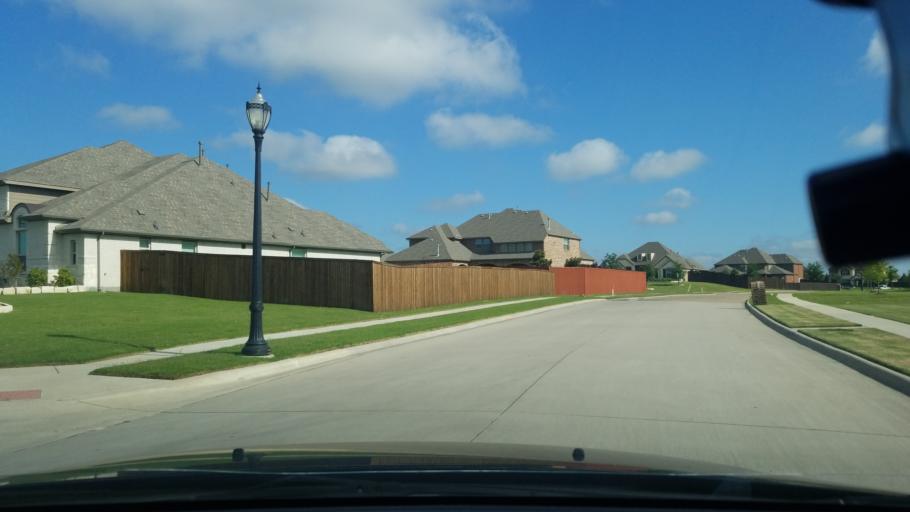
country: US
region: Texas
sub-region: Dallas County
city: Sunnyvale
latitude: 32.8031
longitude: -96.5667
